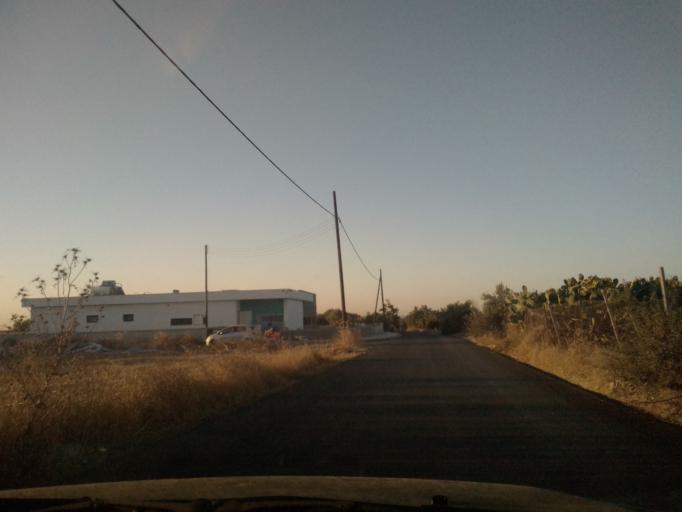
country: CY
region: Limassol
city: Ypsonas
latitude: 34.6757
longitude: 32.9672
